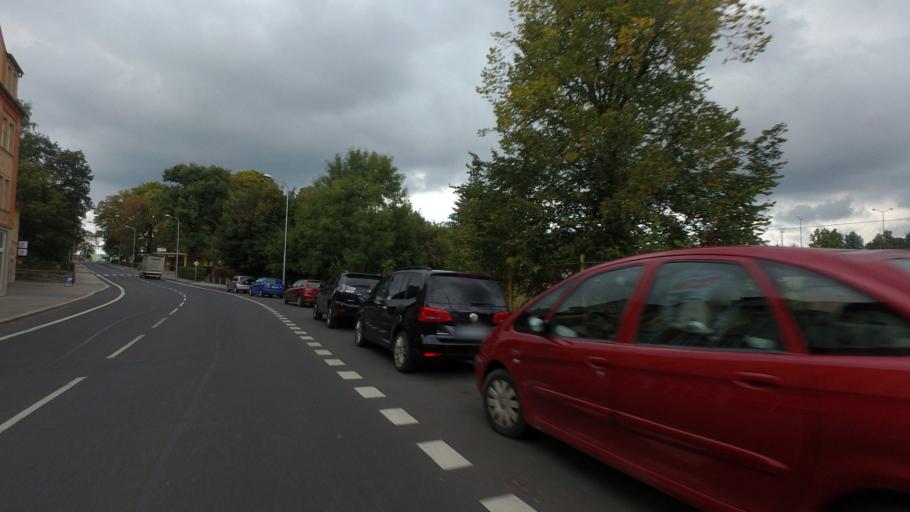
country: CZ
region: Ustecky
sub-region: Okres Decin
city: Rumburk
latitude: 50.9552
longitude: 14.5520
